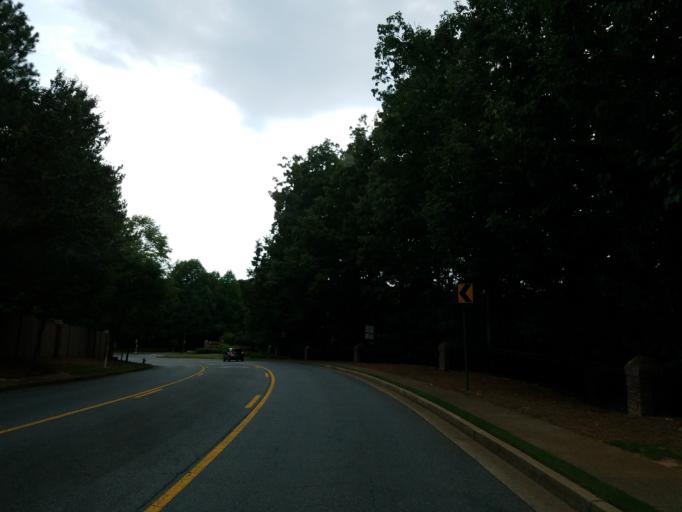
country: US
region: Georgia
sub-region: Cherokee County
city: Woodstock
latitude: 34.0408
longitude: -84.4645
